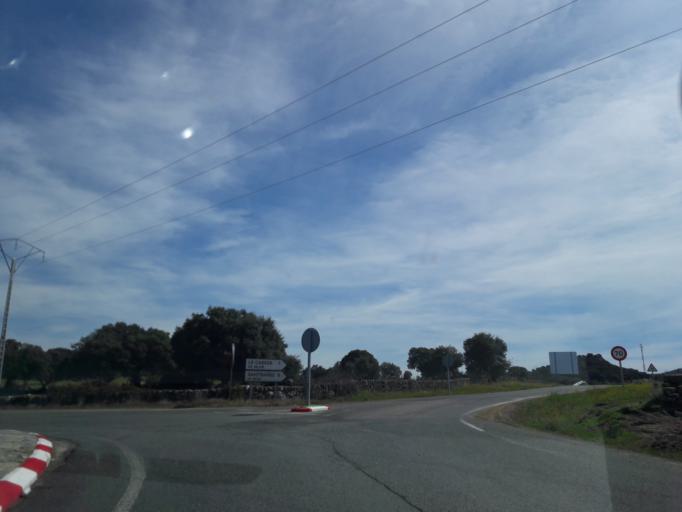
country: ES
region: Castille and Leon
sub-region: Provincia de Salamanca
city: Fuentes de Bejar
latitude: 40.4979
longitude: -5.6738
